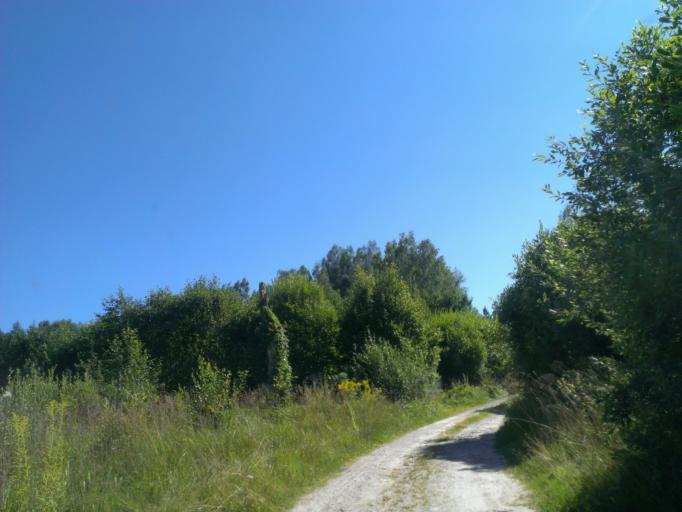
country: LV
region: Incukalns
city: Incukalns
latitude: 57.1270
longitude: 24.7186
